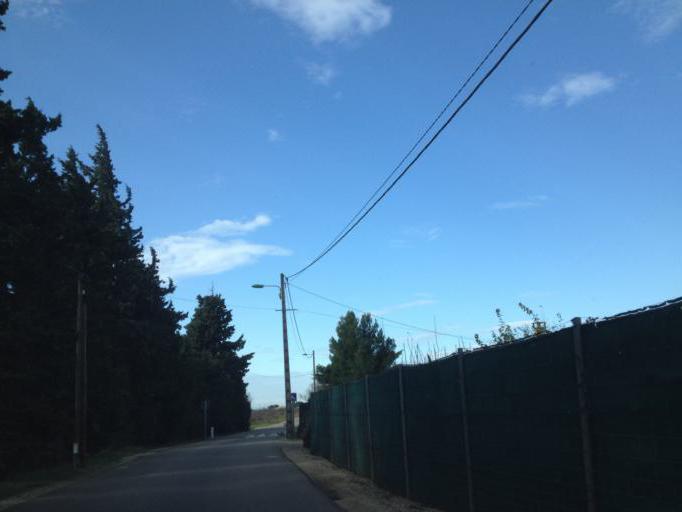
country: FR
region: Provence-Alpes-Cote d'Azur
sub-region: Departement du Vaucluse
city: Sorgues
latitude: 44.0342
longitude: 4.8664
